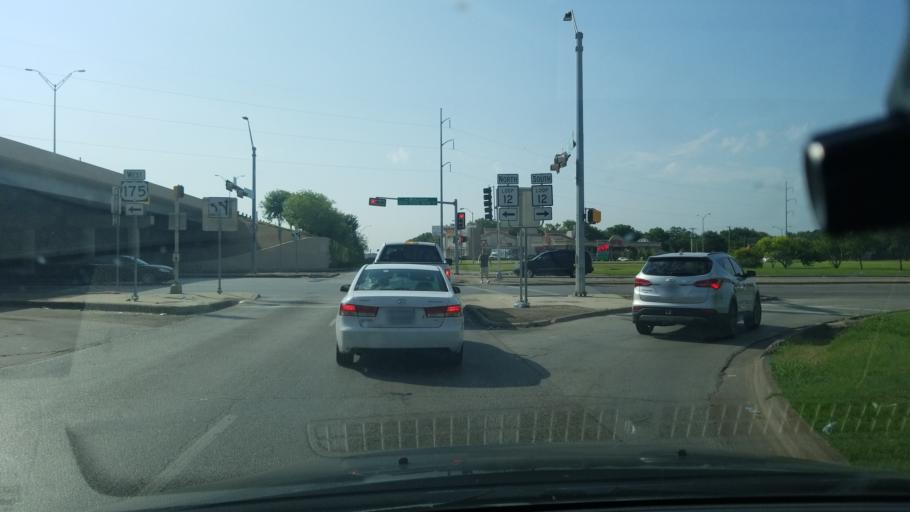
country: US
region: Texas
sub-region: Dallas County
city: Balch Springs
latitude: 32.7132
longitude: -96.6839
